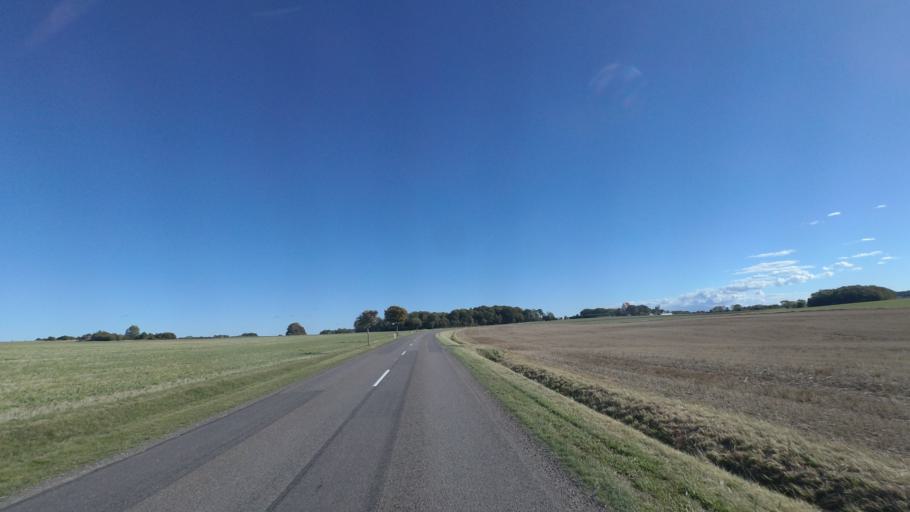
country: DK
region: Capital Region
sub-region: Bornholm Kommune
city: Nexo
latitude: 55.1218
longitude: 15.0983
